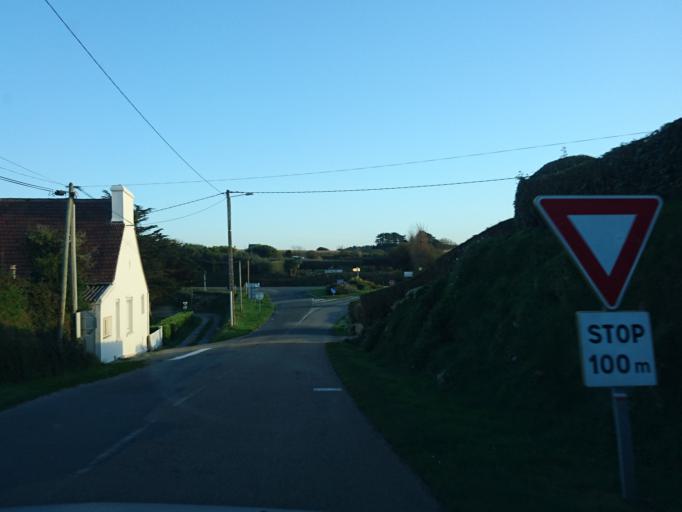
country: FR
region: Brittany
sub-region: Departement du Finistere
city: Landunvez
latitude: 48.5297
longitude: -4.7466
